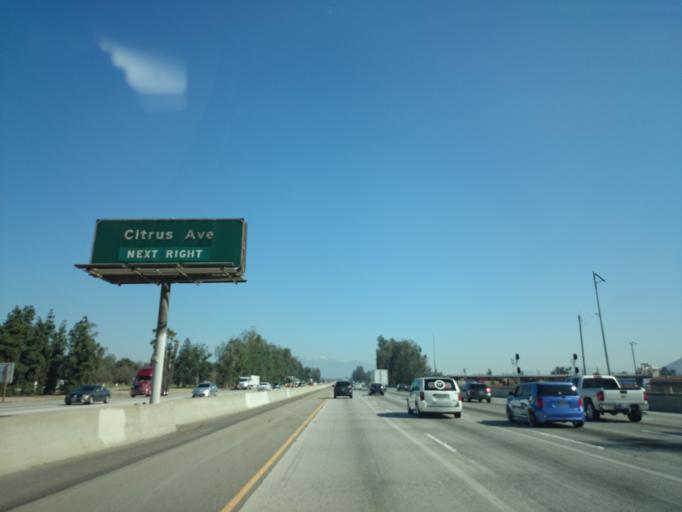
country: US
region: California
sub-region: San Bernardino County
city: Fontana
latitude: 34.0662
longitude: -117.4712
